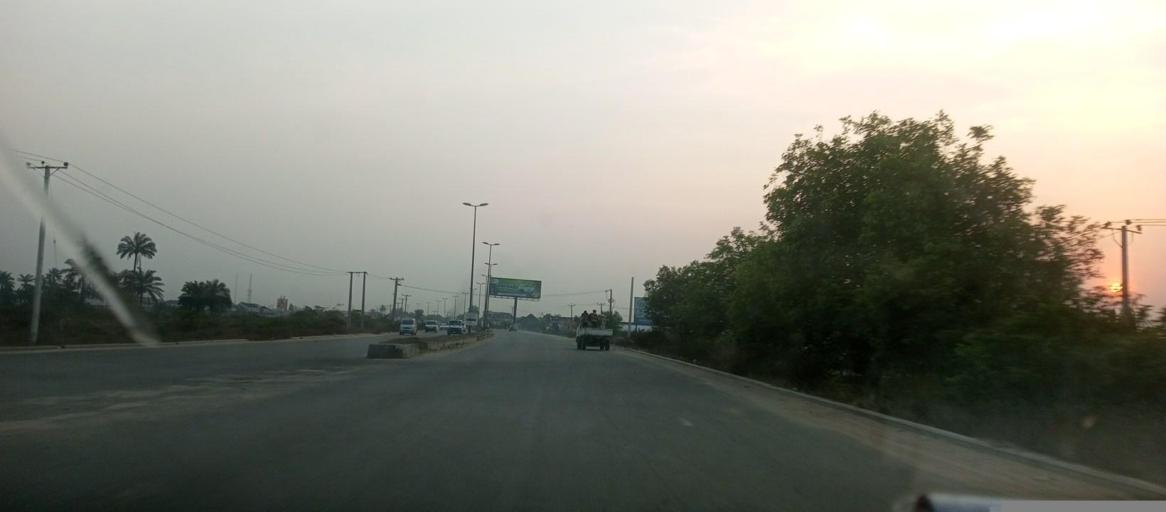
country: NG
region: Rivers
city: Emuoha
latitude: 4.9280
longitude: 6.9997
